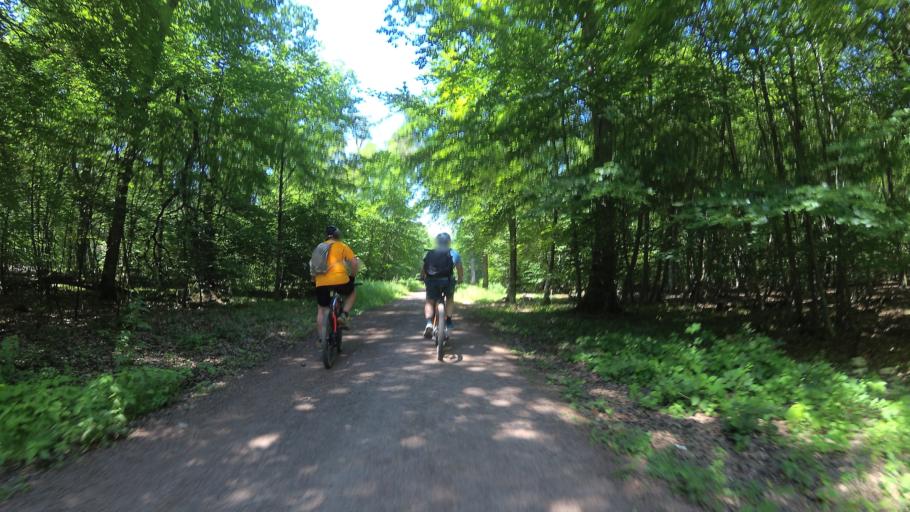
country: DE
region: Saarland
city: Saarwellingen
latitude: 49.3661
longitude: 6.8097
